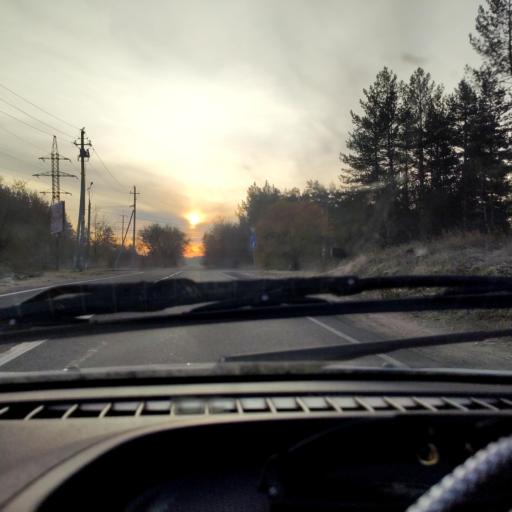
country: RU
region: Samara
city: Zhigulevsk
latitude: 53.5048
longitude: 49.4625
